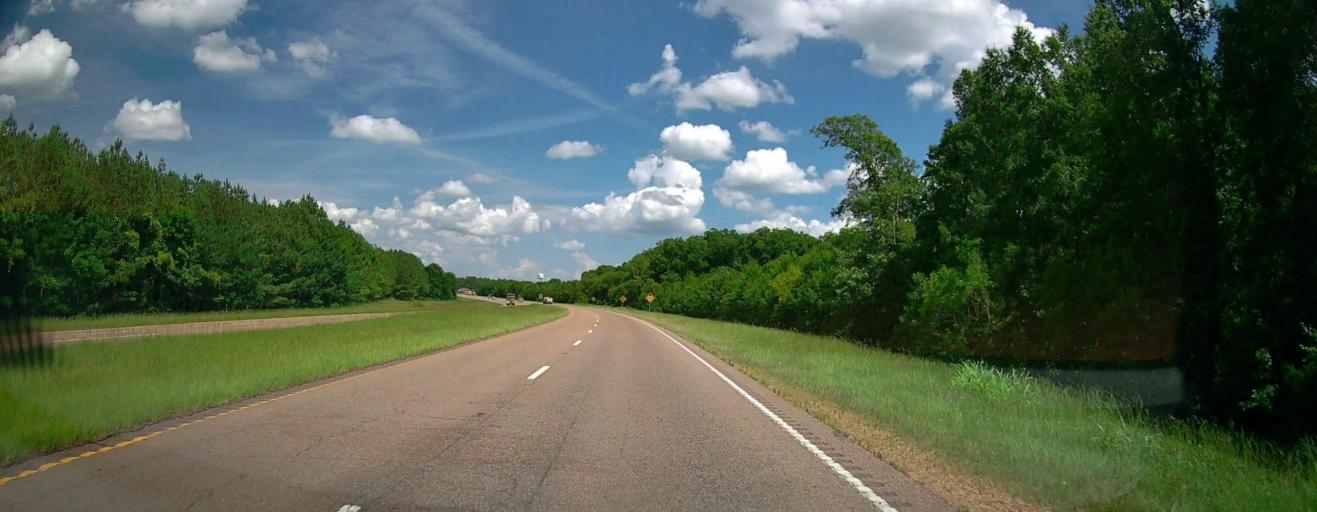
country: US
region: Mississippi
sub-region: Monroe County
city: Aberdeen
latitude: 33.8158
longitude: -88.5757
